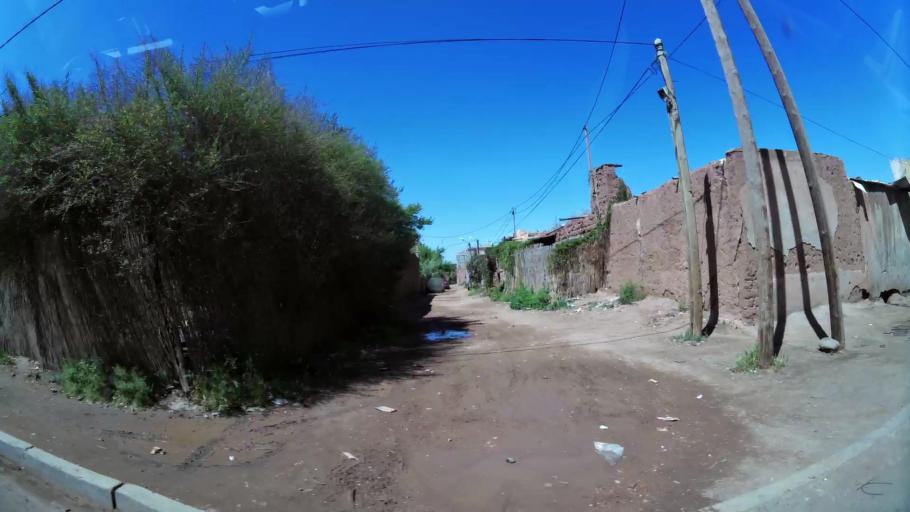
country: MA
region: Marrakech-Tensift-Al Haouz
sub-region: Marrakech
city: Marrakesh
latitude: 31.6302
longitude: -8.0702
